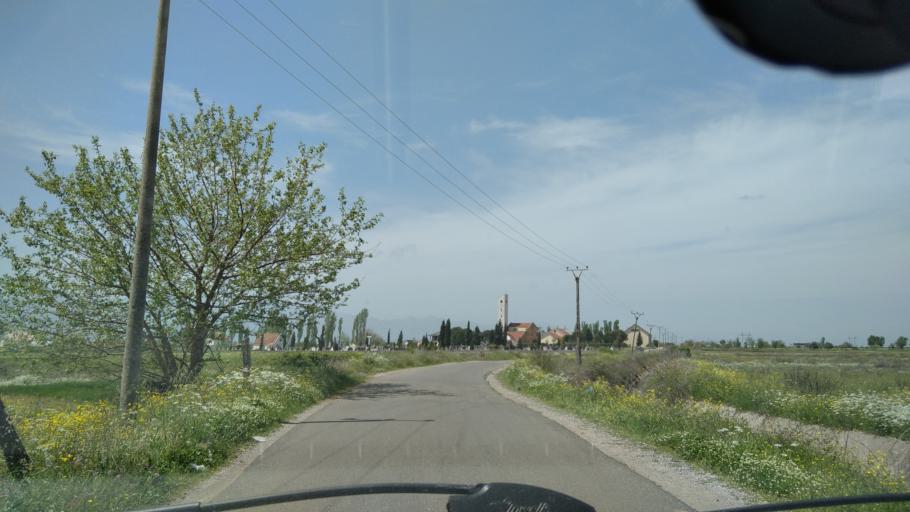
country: AL
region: Shkoder
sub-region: Rrethi i Malesia e Madhe
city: Gruemire
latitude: 42.1425
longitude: 19.5061
